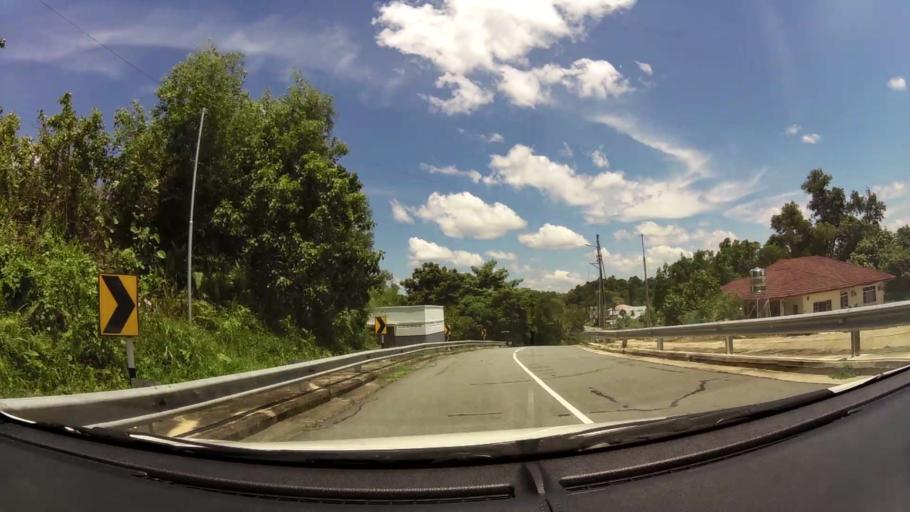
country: BN
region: Brunei and Muara
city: Bandar Seri Begawan
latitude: 4.9393
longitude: 114.9658
